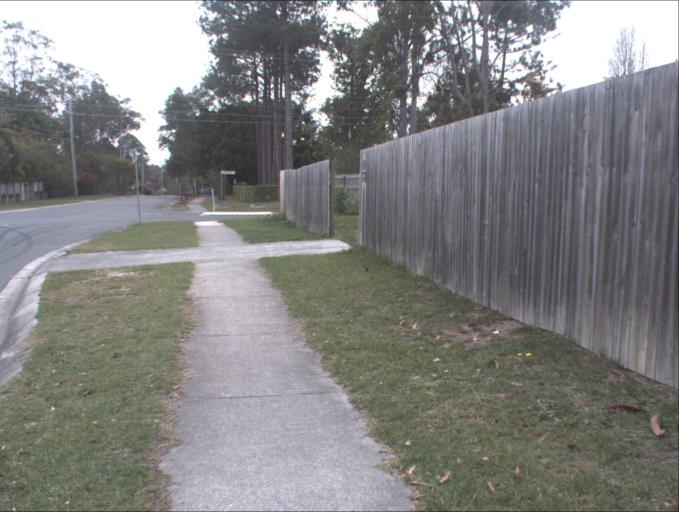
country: AU
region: Queensland
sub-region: Logan
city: Waterford West
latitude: -27.6794
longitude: 153.1240
